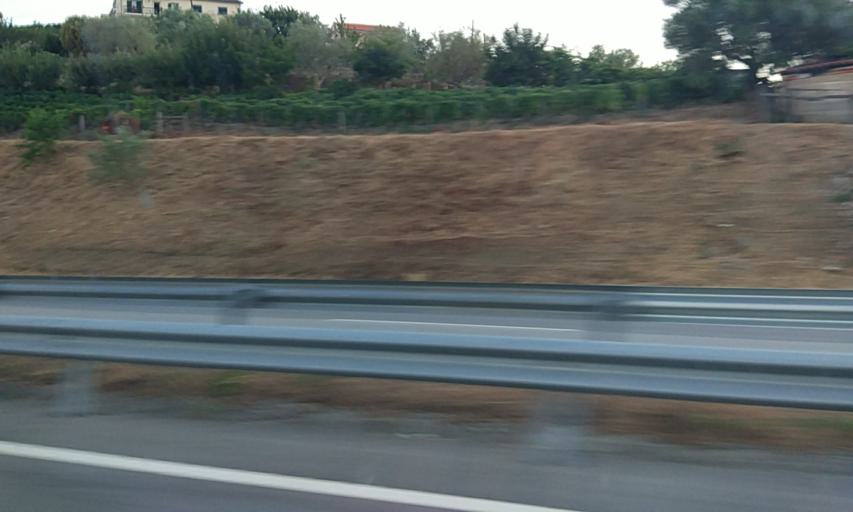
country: PT
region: Vila Real
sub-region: Santa Marta de Penaguiao
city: Santa Marta de Penaguiao
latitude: 41.2236
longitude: -7.7331
